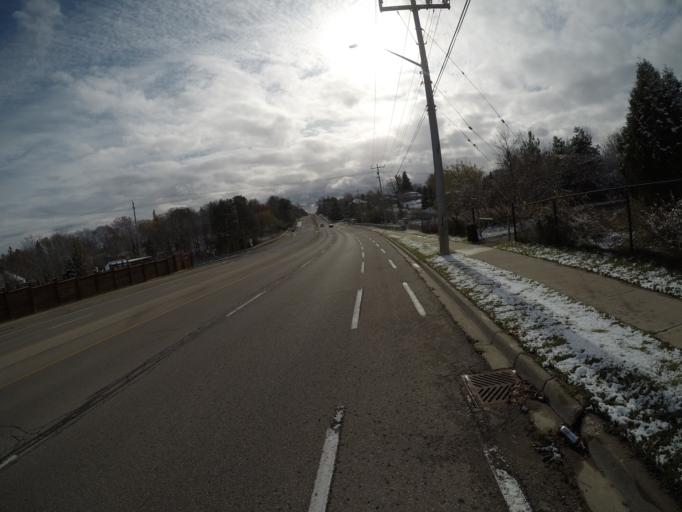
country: CA
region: Ontario
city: Waterloo
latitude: 43.5056
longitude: -80.4973
